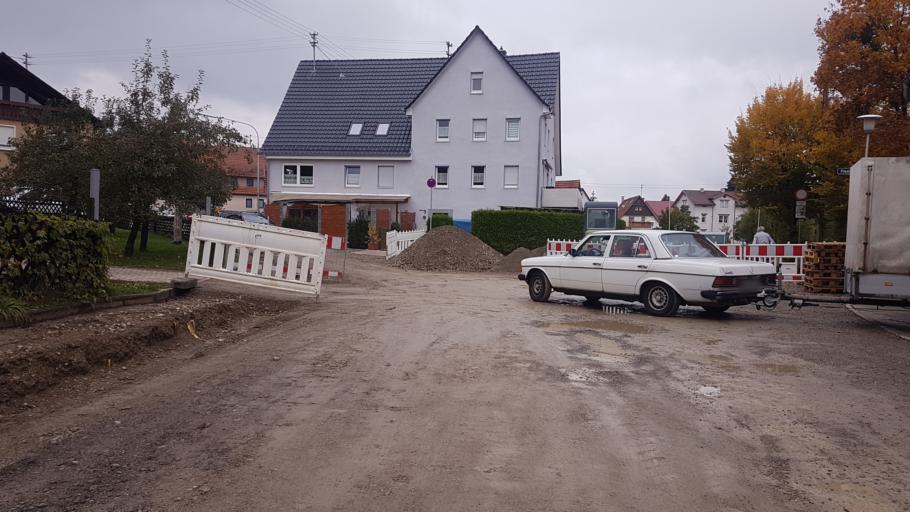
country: DE
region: Baden-Wuerttemberg
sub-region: Tuebingen Region
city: Ofterdingen
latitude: 48.4229
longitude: 9.0355
